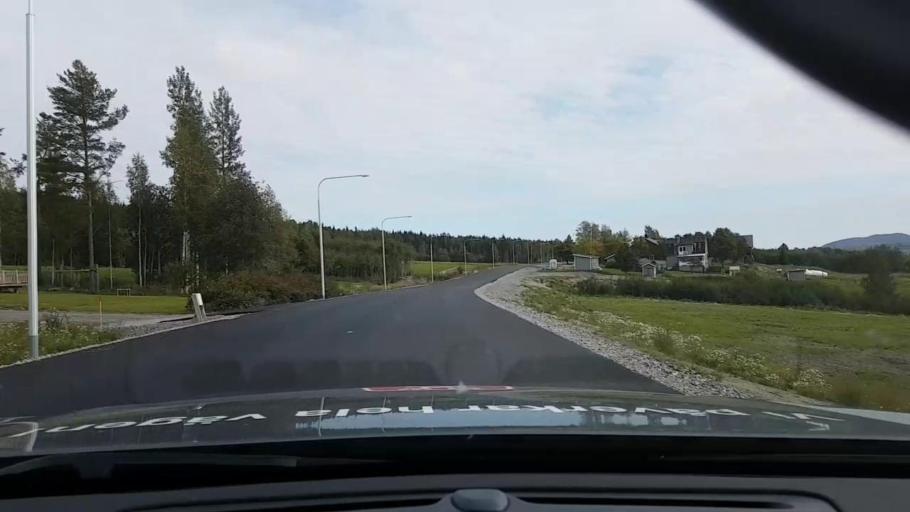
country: SE
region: Vaesternorrland
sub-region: OErnskoeldsviks Kommun
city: Bjasta
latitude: 63.2930
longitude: 18.4716
